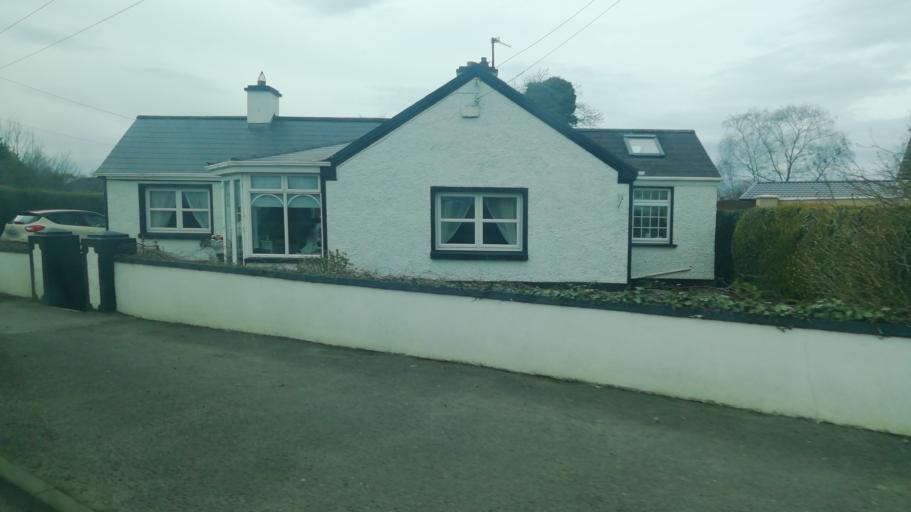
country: IE
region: Leinster
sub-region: Uibh Fhaili
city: Edenderry
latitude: 53.3313
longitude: -7.0725
